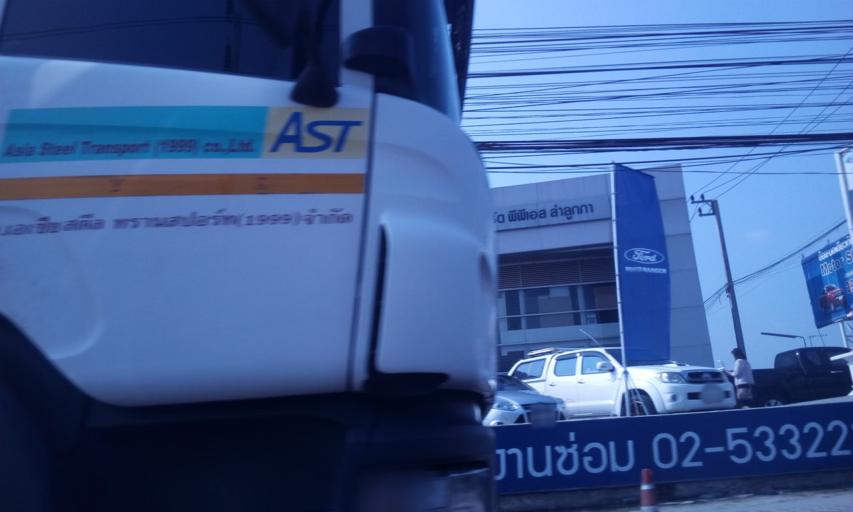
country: TH
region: Bangkok
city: Sai Mai
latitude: 13.9325
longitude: 100.6801
